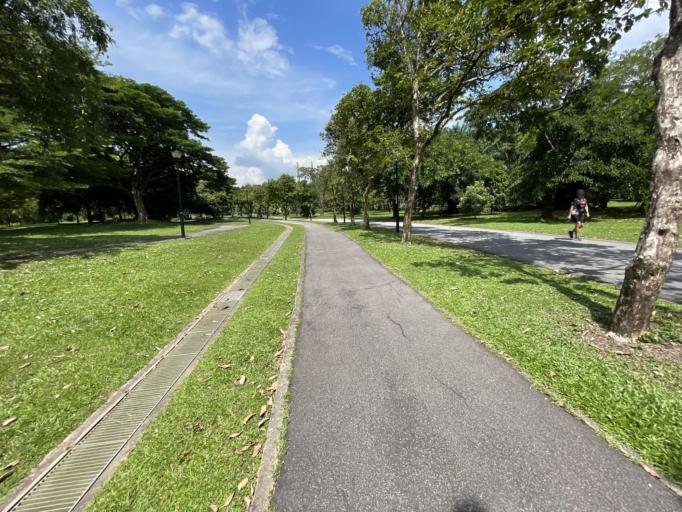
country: SG
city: Singapore
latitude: 1.2952
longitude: 103.7641
